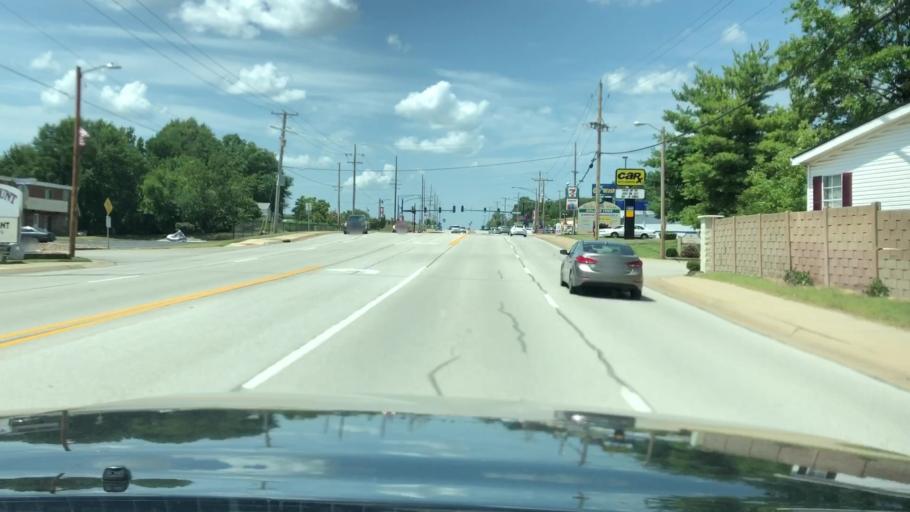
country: US
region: Missouri
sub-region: Saint Charles County
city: Saint Peters
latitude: 38.7882
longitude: -90.6135
